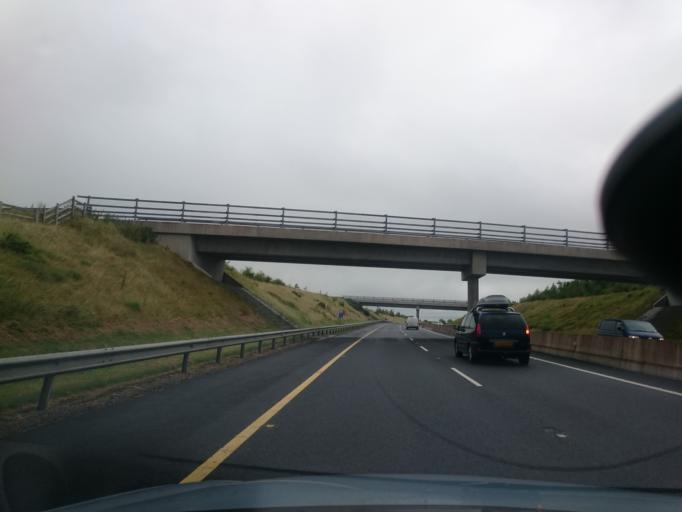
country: IE
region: Leinster
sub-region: Kildare
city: Castledermot
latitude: 52.9257
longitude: -6.8665
